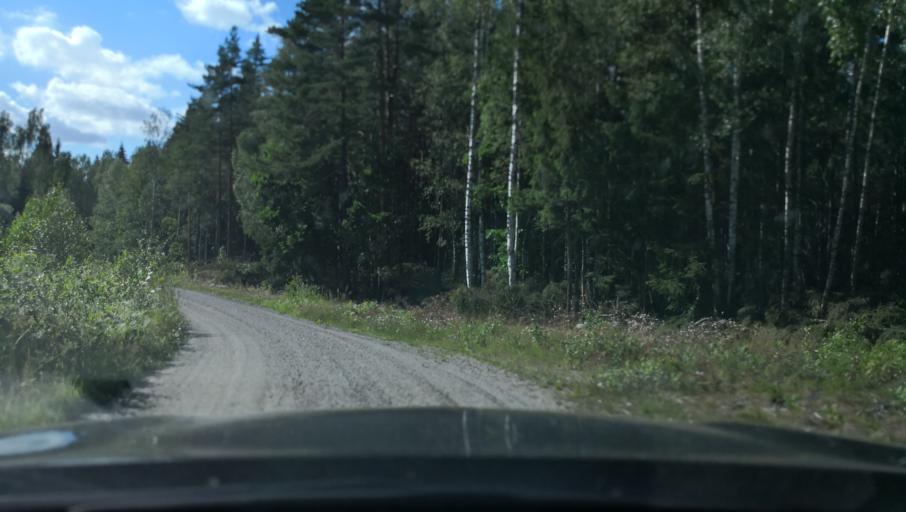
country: SE
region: Vaestmanland
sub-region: Arboga Kommun
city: Tyringe
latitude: 59.3496
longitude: 16.0056
